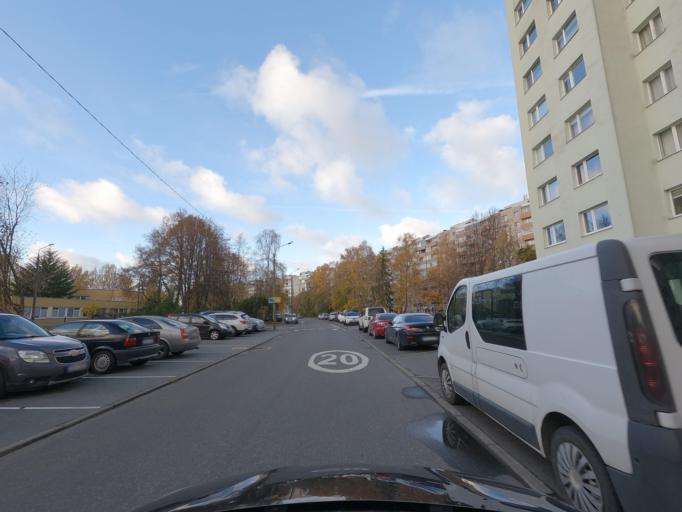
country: EE
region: Harju
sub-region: Saue vald
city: Laagri
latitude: 59.4159
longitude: 24.6513
